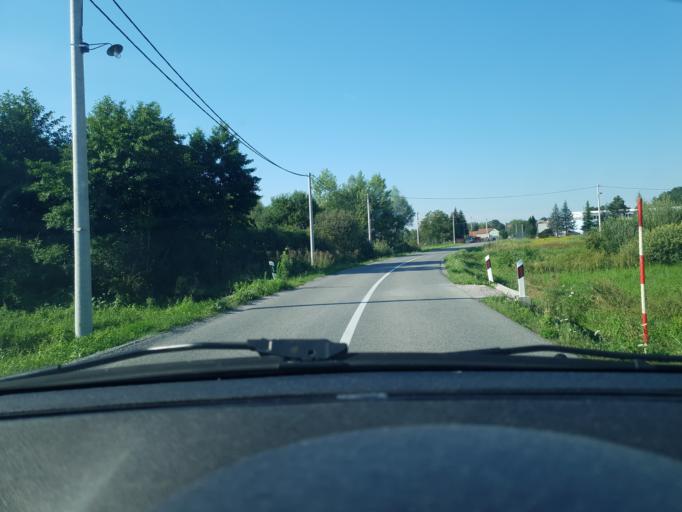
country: HR
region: Zagrebacka
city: Jakovlje
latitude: 45.9270
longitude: 15.8426
